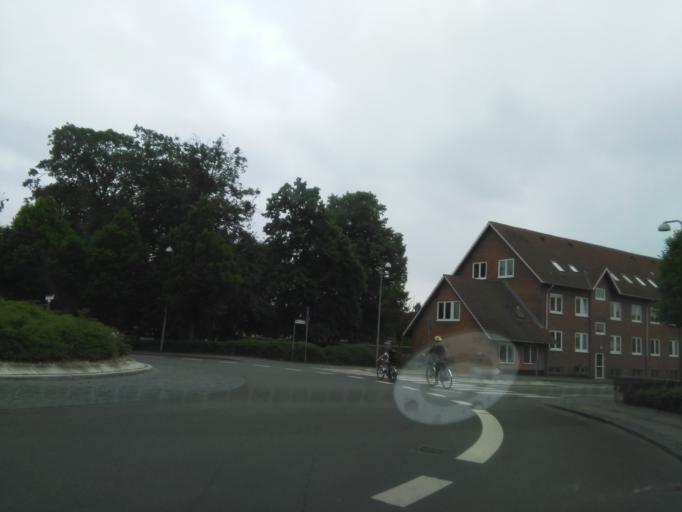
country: DK
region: Capital Region
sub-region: Bornholm Kommune
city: Ronne
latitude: 55.0949
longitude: 14.7029
